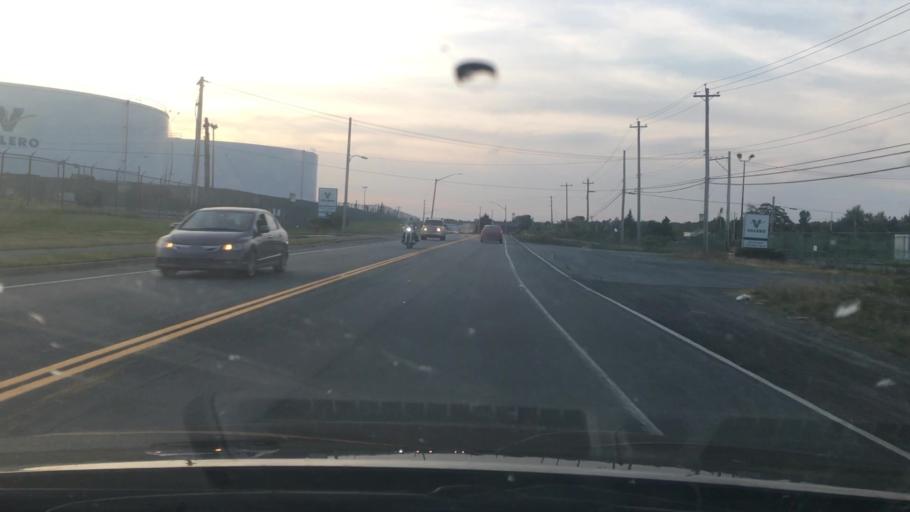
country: CA
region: Nova Scotia
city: Cole Harbour
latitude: 44.6181
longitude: -63.5018
